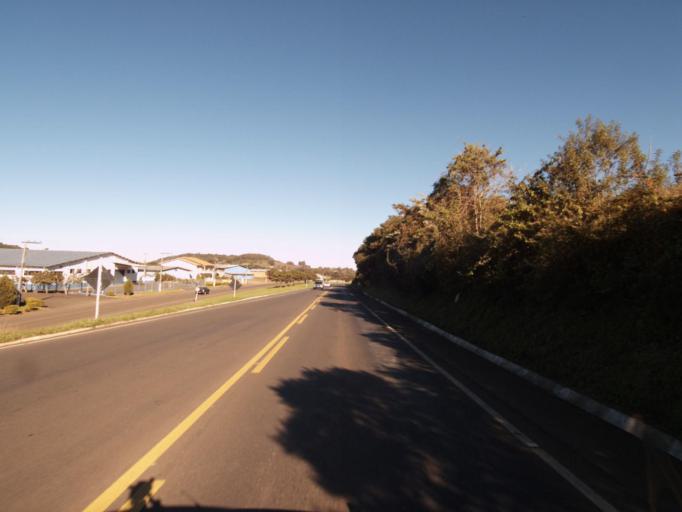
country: BR
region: Santa Catarina
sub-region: Chapeco
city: Chapeco
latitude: -26.9889
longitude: -52.6106
